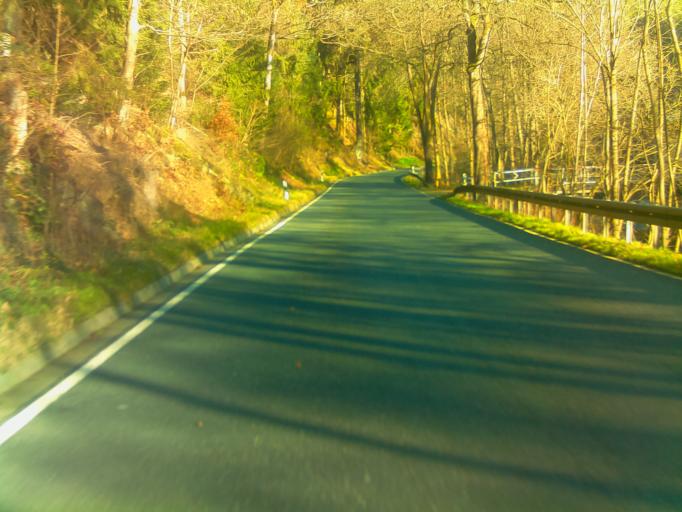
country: DE
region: Thuringia
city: Oberweissbach
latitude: 50.6079
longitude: 11.1403
